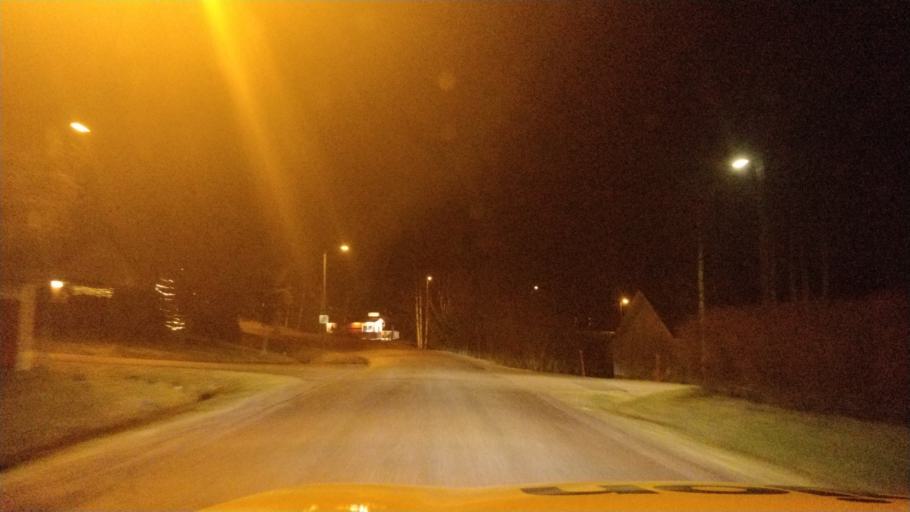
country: FI
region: Uusimaa
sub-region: Helsinki
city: Nurmijaervi
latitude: 60.3815
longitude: 24.6950
